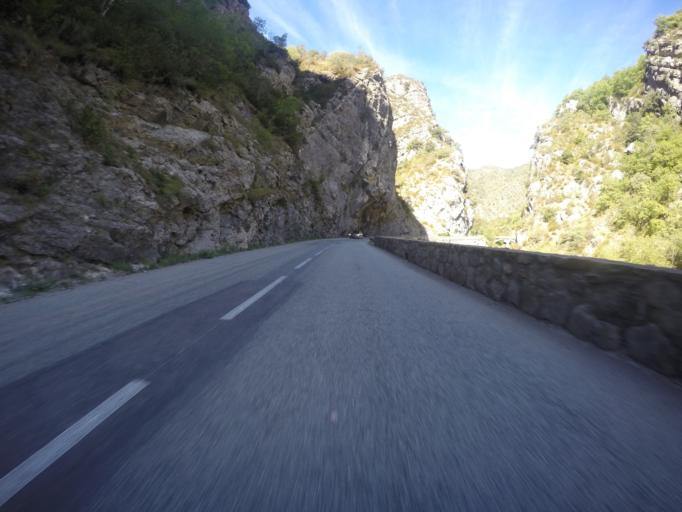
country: FR
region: Provence-Alpes-Cote d'Azur
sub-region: Departement des Alpes-Maritimes
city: Gilette
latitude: 43.9378
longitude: 7.1685
